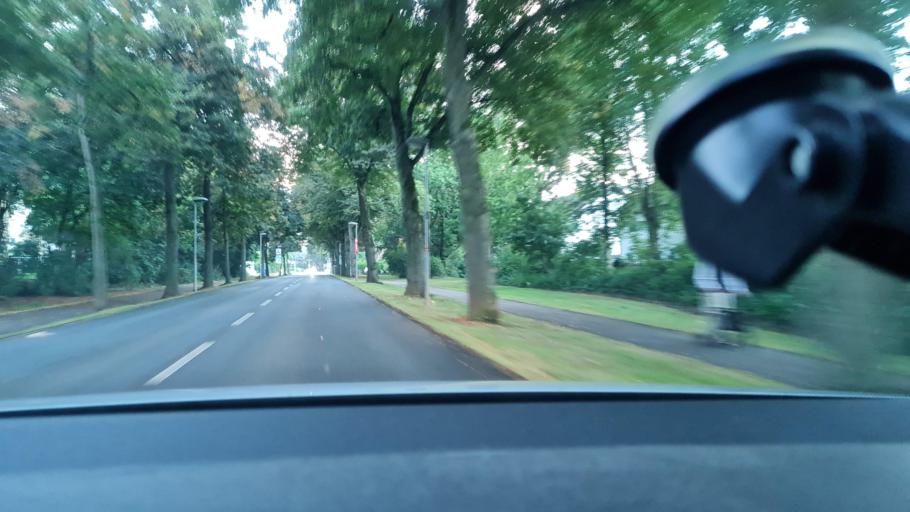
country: DE
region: North Rhine-Westphalia
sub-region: Regierungsbezirk Dusseldorf
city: Moers
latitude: 51.4788
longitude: 6.6254
